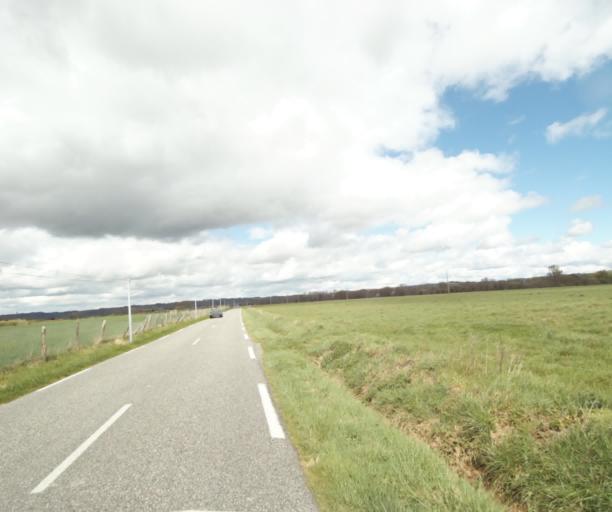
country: FR
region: Midi-Pyrenees
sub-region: Departement de la Haute-Garonne
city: Calmont
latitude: 43.2497
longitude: 1.6365
